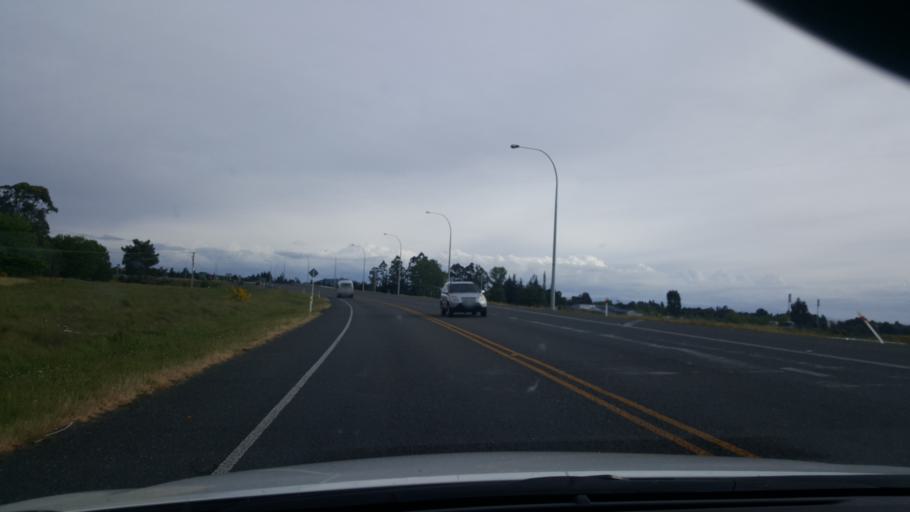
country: NZ
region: Waikato
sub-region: Taupo District
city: Taupo
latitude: -38.6643
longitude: 176.1012
